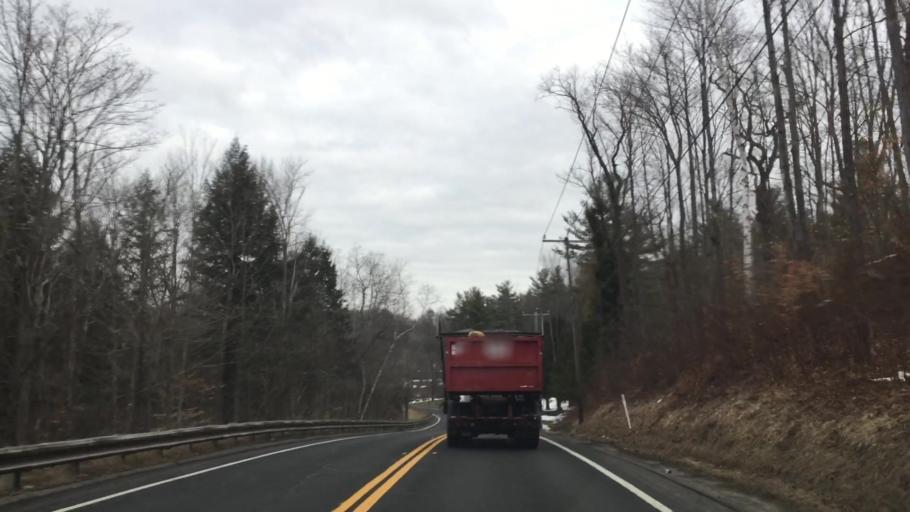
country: US
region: Massachusetts
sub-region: Berkshire County
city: Hinsdale
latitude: 42.4601
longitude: -73.1317
